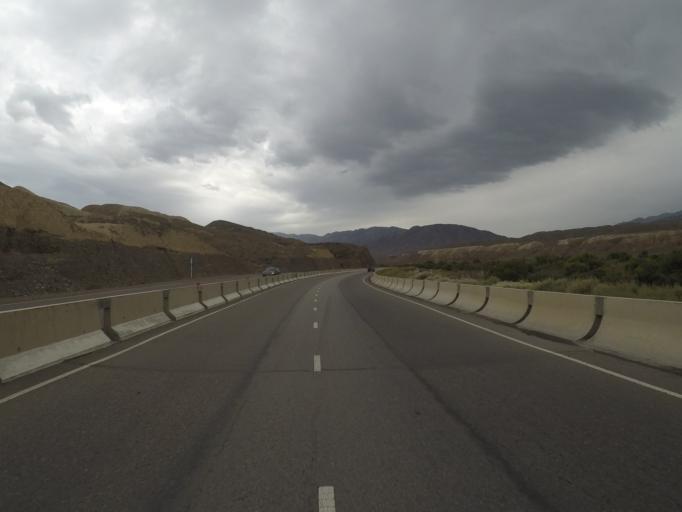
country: KG
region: Naryn
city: Kochkor
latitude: 42.5048
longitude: 75.8370
